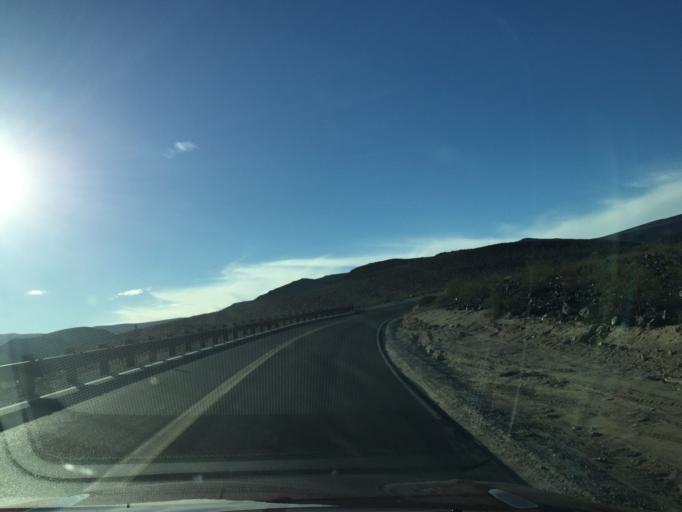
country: US
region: California
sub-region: San Bernardino County
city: Searles Valley
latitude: 36.3401
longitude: -117.5115
